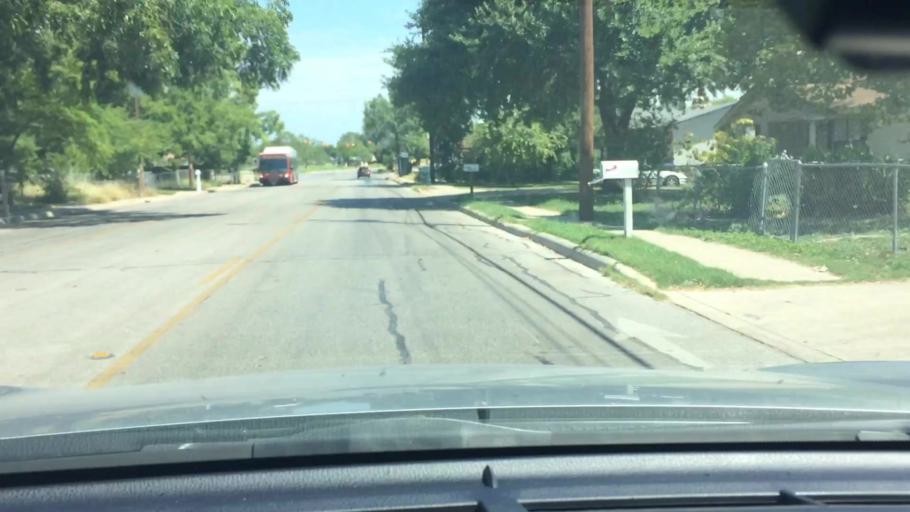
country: US
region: Texas
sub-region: Bexar County
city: San Antonio
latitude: 29.3948
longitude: -98.4332
